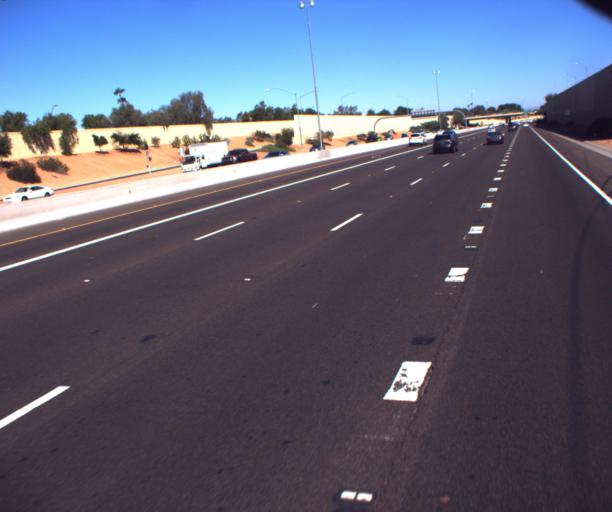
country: US
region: Arizona
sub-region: Maricopa County
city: Tempe
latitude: 33.3737
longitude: -111.8932
